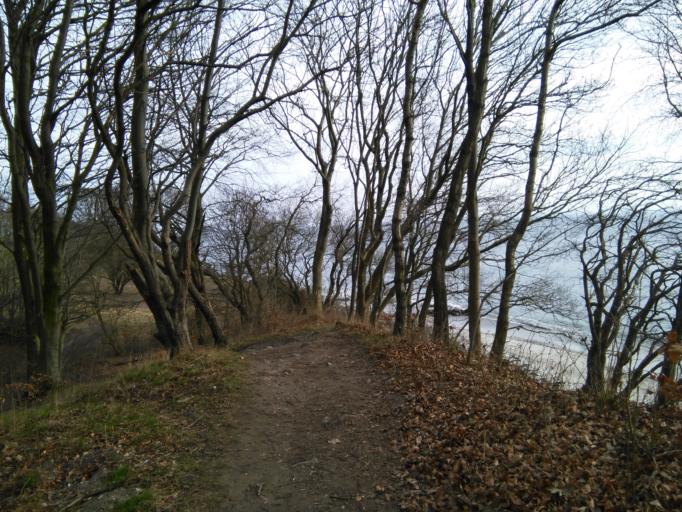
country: DK
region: Central Jutland
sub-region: Arhus Kommune
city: Beder
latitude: 56.0909
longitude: 10.2481
